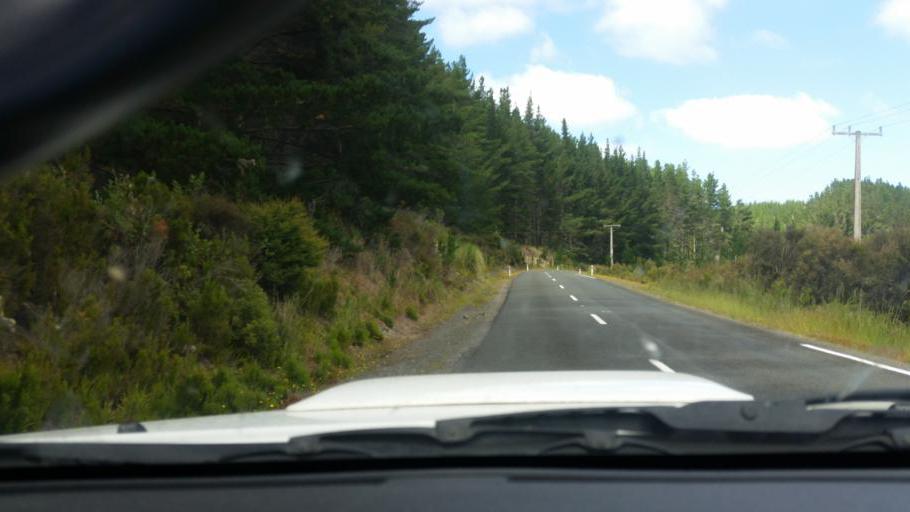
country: NZ
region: Northland
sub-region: Kaipara District
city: Dargaville
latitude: -35.8211
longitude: 173.7101
